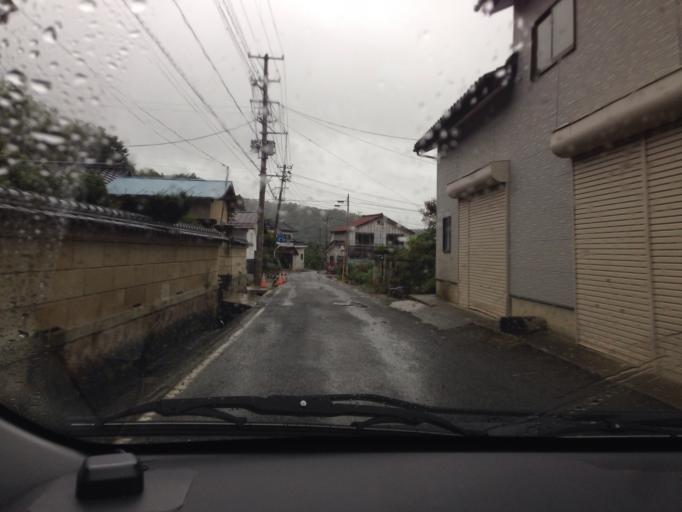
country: JP
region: Fukushima
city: Koriyama
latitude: 37.4497
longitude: 140.2759
